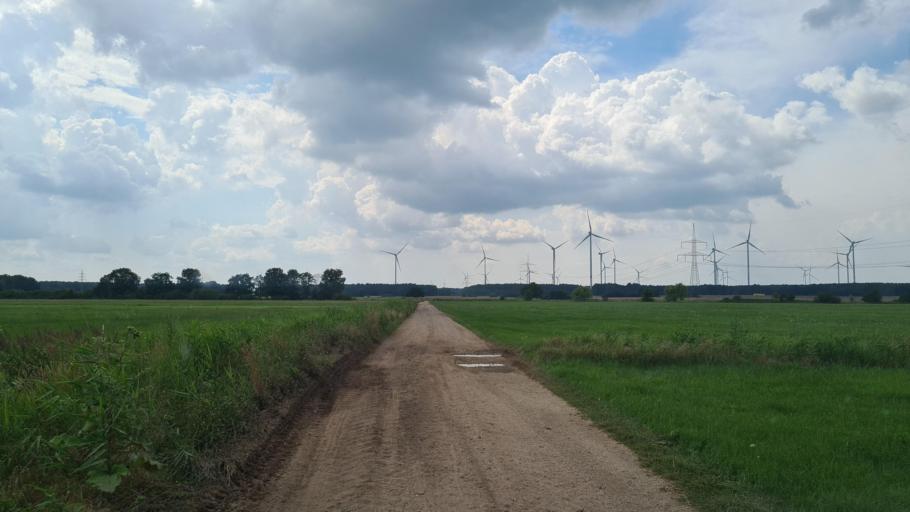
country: DE
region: Brandenburg
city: Sallgast
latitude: 51.6262
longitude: 13.8612
